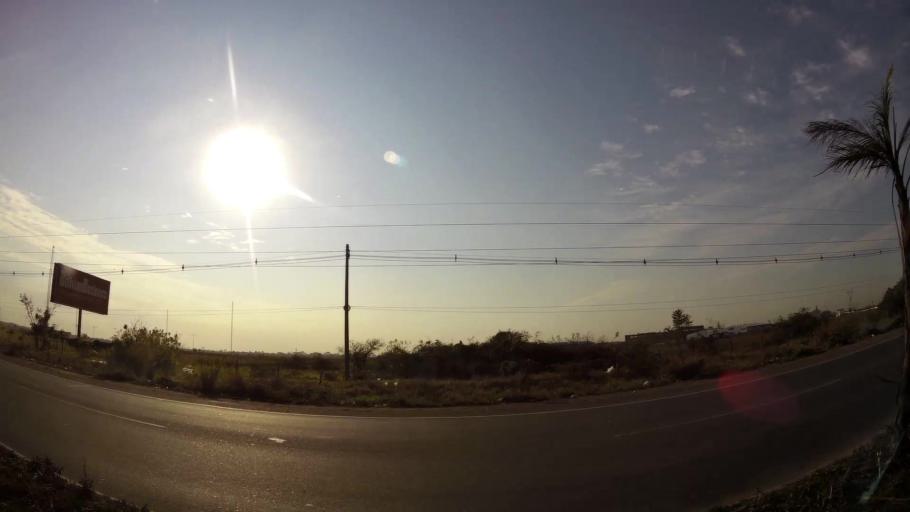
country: BO
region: Santa Cruz
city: Santa Cruz de la Sierra
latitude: -17.6733
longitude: -63.1585
